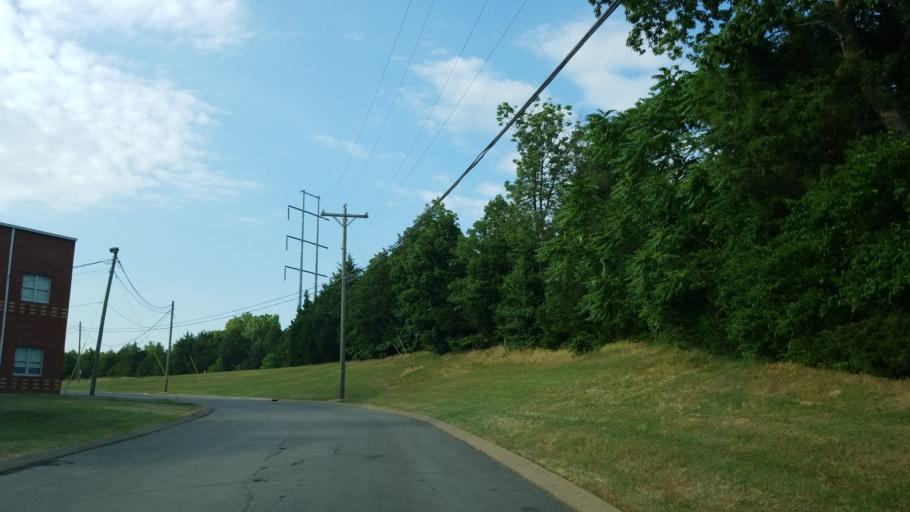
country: US
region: Tennessee
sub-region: Rutherford County
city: La Vergne
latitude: 36.0406
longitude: -86.6029
